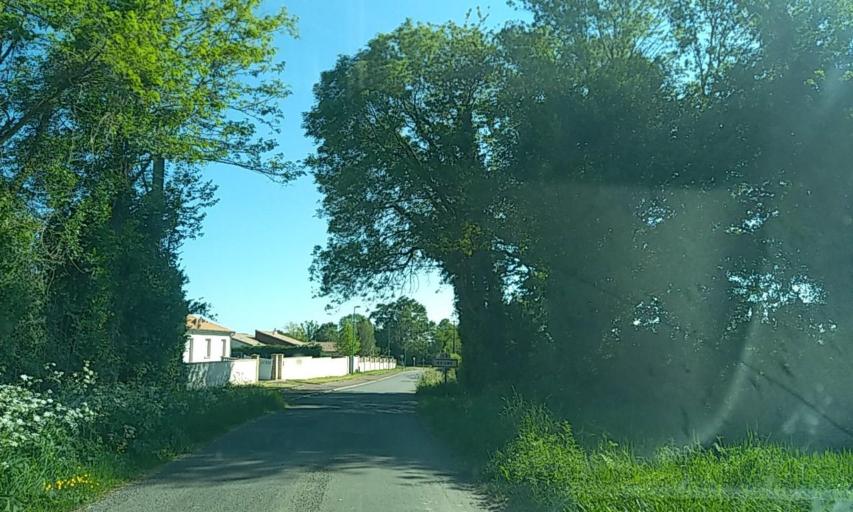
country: FR
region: Poitou-Charentes
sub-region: Departement des Deux-Sevres
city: Boisme
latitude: 46.7803
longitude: -0.4274
